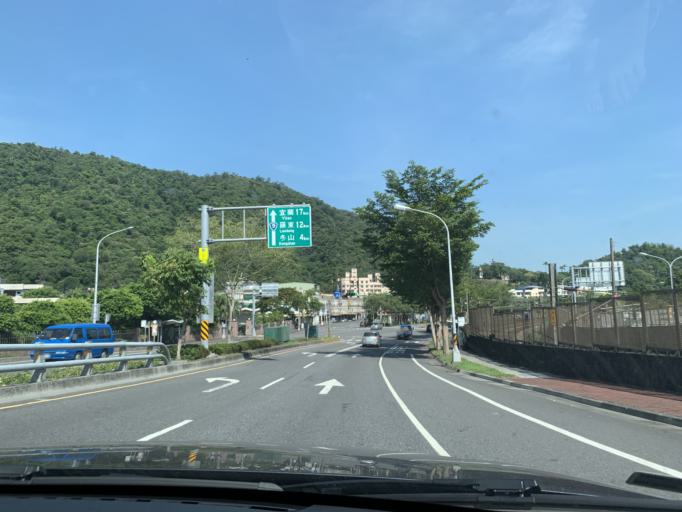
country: TW
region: Taiwan
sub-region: Yilan
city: Yilan
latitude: 24.5967
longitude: 121.8355
